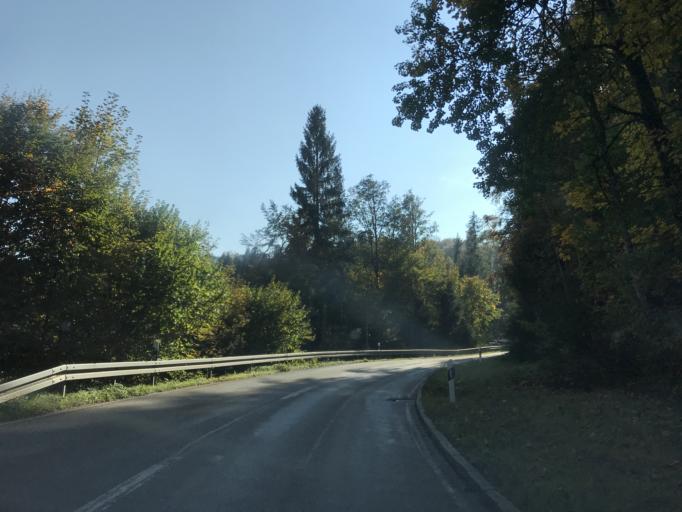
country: DE
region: Baden-Wuerttemberg
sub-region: Freiburg Region
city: Gorwihl
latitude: 47.6267
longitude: 8.0511
